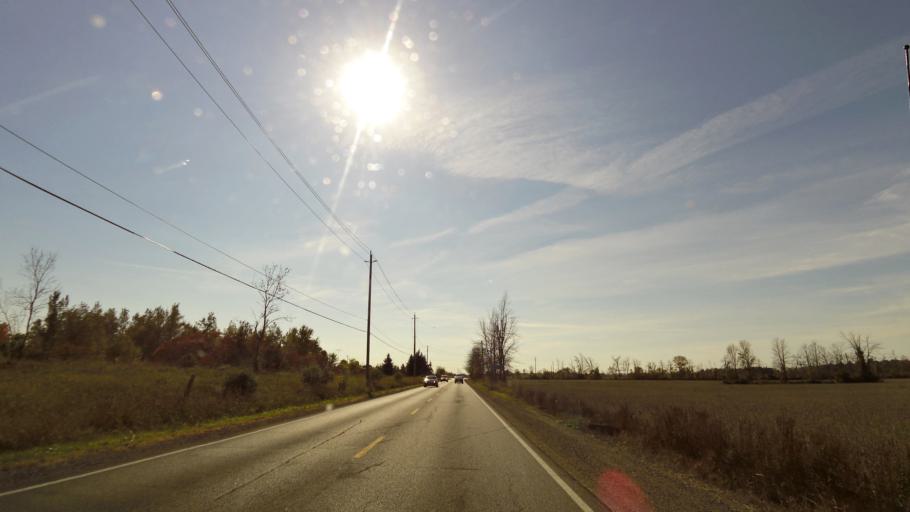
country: CA
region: Ontario
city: Mississauga
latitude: 43.5477
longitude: -79.7678
